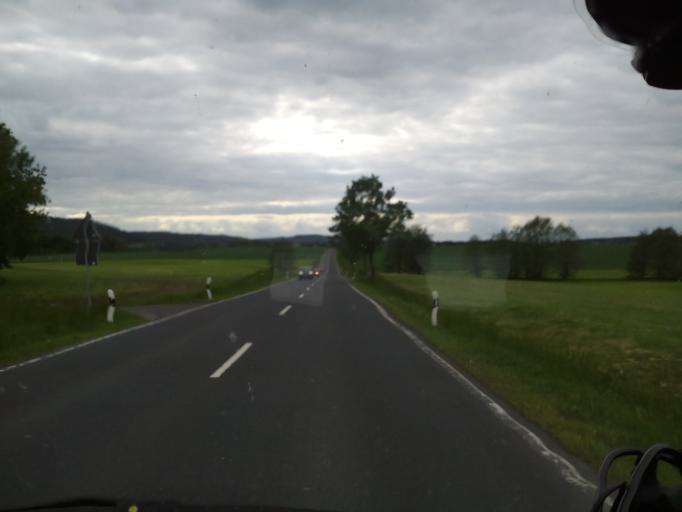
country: DE
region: Thuringia
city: Veilsdorf
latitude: 50.4164
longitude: 10.7979
